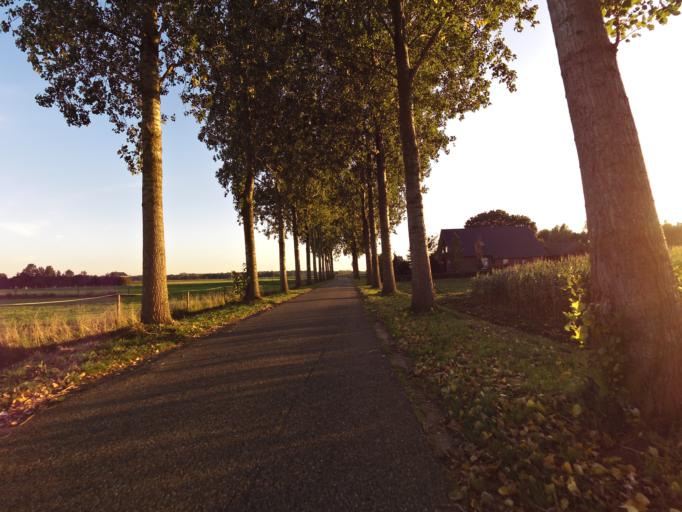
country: NL
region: Gelderland
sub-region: Gemeente Zevenaar
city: Zevenaar
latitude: 51.9240
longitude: 6.1592
